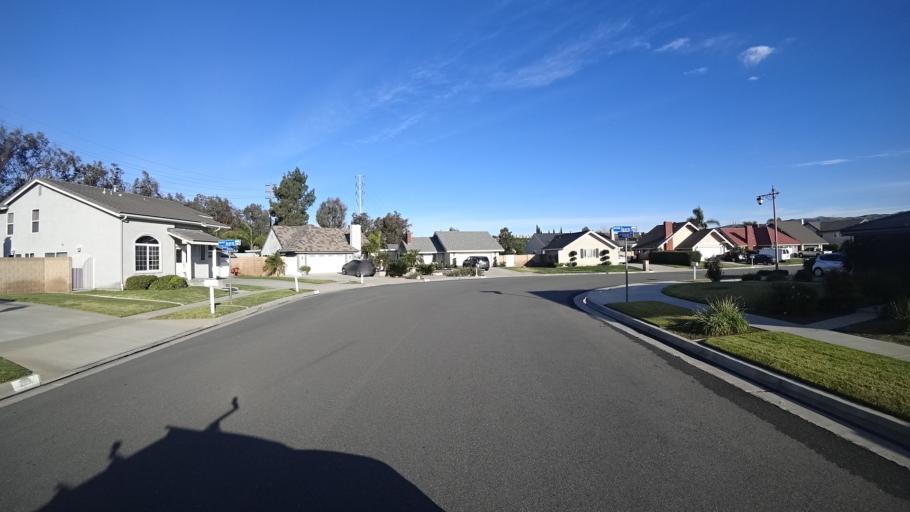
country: US
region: California
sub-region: Orange County
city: Yorba Linda
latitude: 33.8604
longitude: -117.7726
